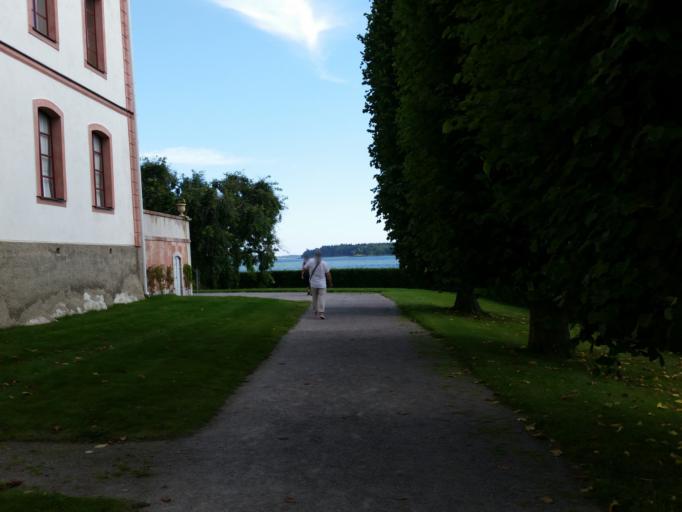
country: SE
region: Soedermanland
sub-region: Trosa Kommun
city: Trosa
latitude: 58.9499
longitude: 17.5842
